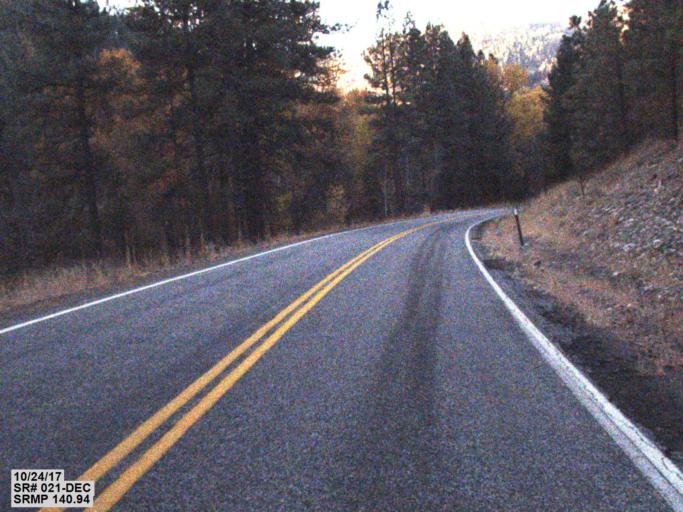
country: US
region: Washington
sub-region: Ferry County
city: Republic
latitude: 48.3979
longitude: -118.7334
